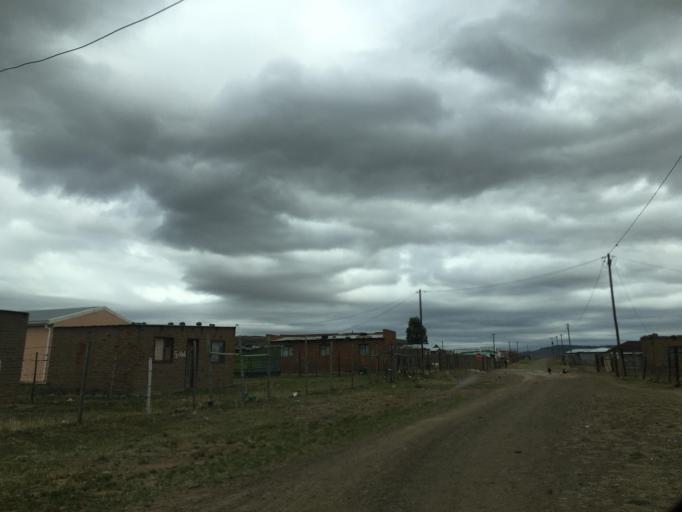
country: ZA
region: Eastern Cape
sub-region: Chris Hani District Municipality
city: Cala
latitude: -31.5381
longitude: 27.7004
